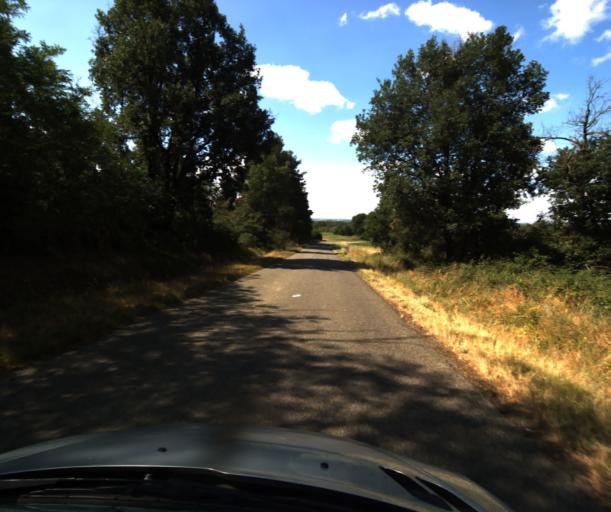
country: FR
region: Midi-Pyrenees
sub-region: Departement du Tarn-et-Garonne
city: Finhan
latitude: 43.9058
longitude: 1.2691
